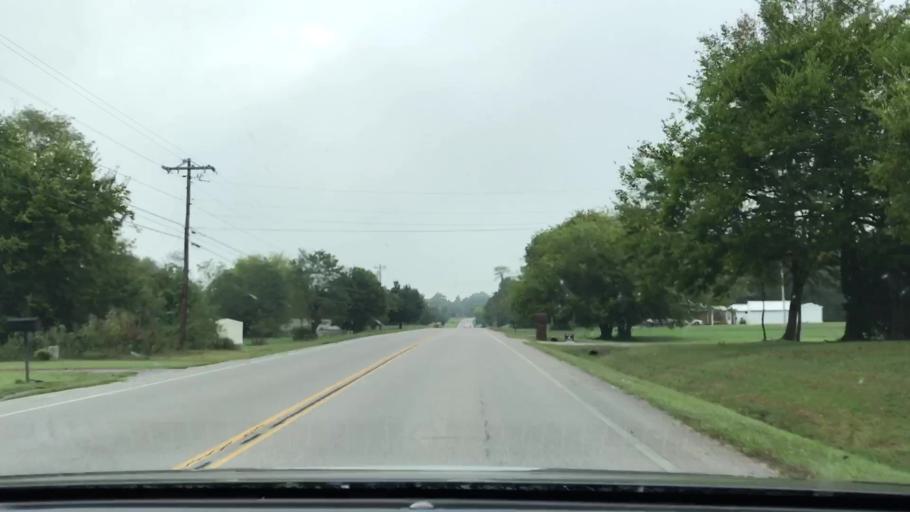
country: US
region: Tennessee
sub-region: Sumner County
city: Portland
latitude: 36.4919
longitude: -86.4943
